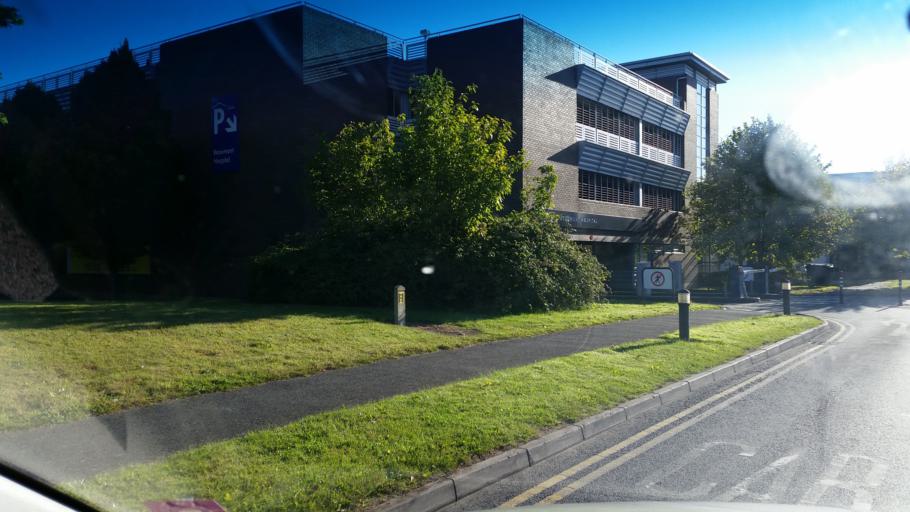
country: IE
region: Leinster
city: Artane
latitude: 53.3887
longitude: -6.2251
